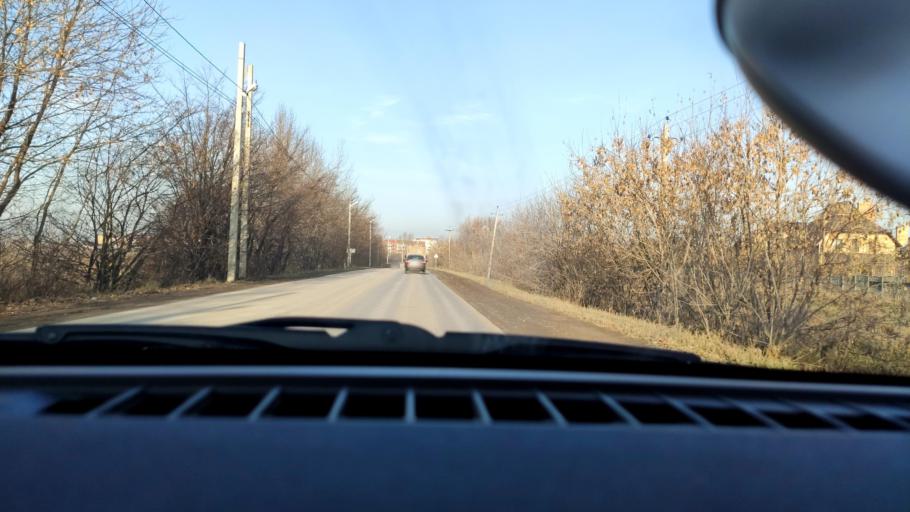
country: RU
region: Perm
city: Kondratovo
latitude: 57.9689
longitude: 56.1160
